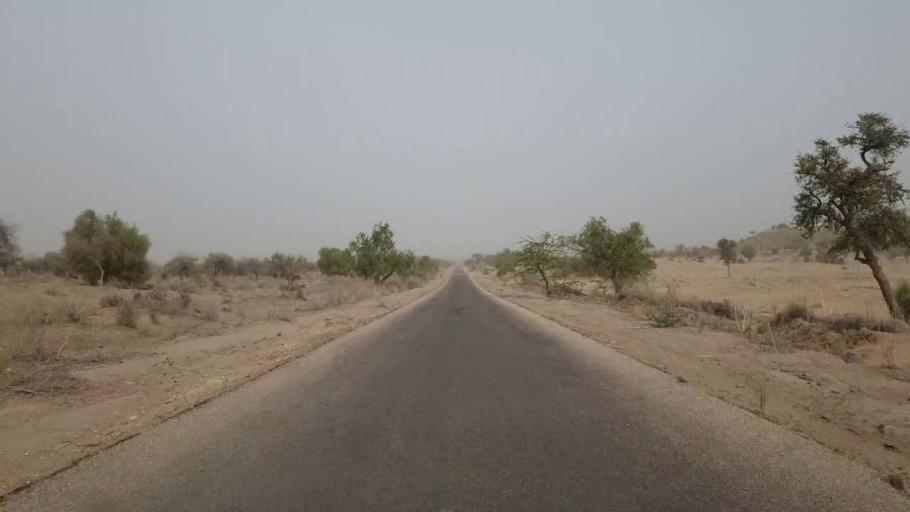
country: PK
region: Sindh
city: Islamkot
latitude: 24.5791
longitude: 70.3061
